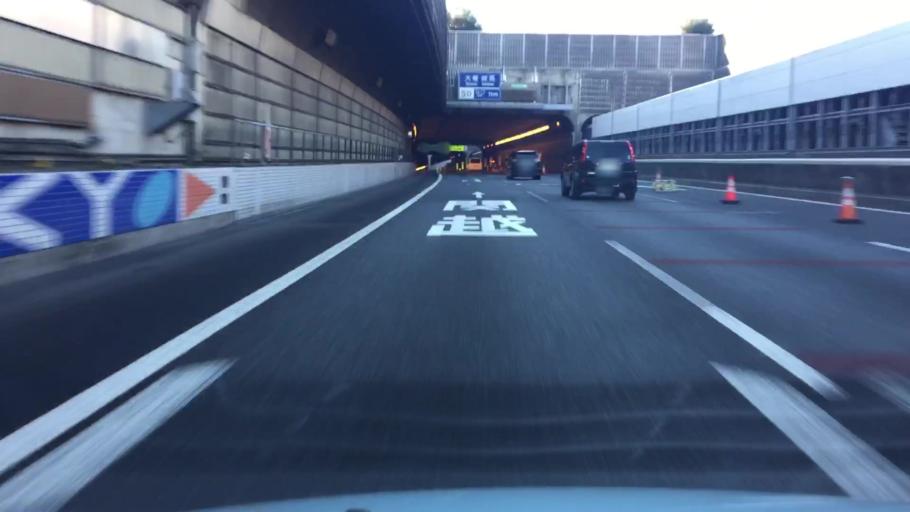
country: JP
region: Saitama
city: Wako
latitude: 35.7705
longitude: 139.6019
